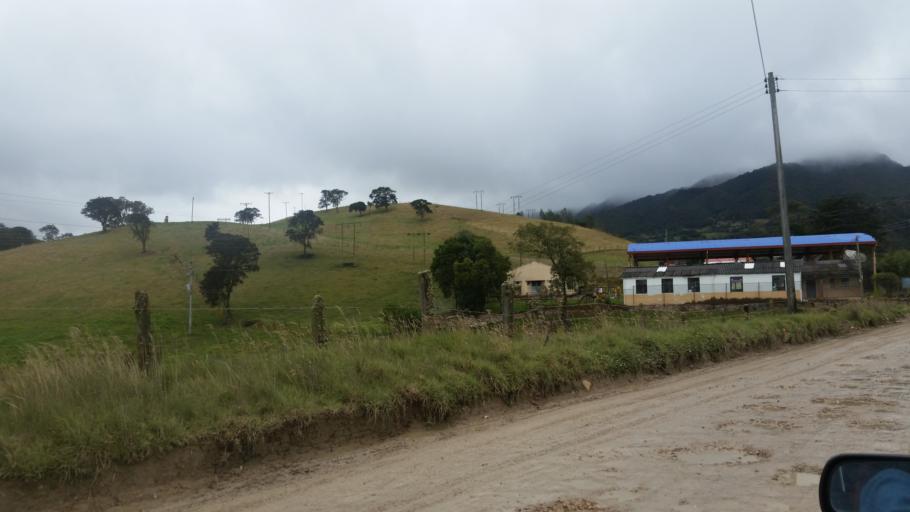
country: CO
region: Cundinamarca
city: La Calera
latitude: 4.7257
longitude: -73.9149
